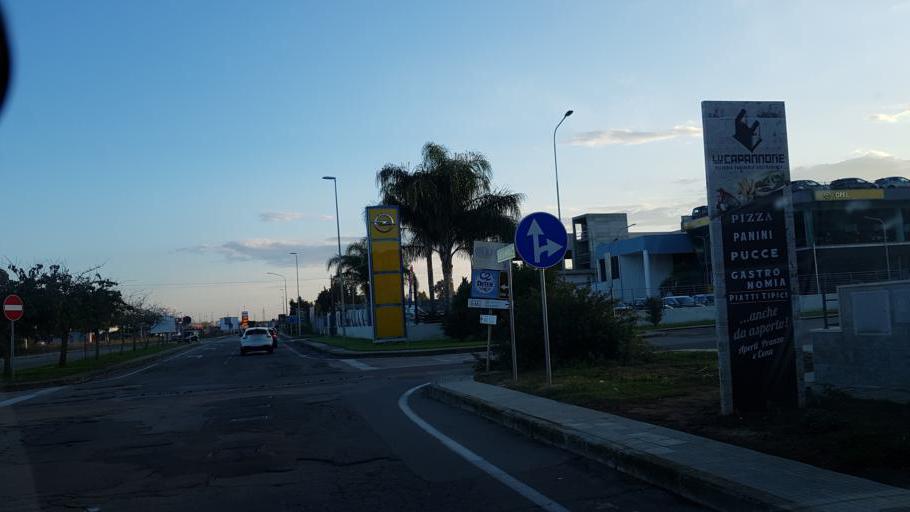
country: IT
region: Apulia
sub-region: Provincia di Lecce
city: Giorgilorio
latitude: 40.3794
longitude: 18.1399
